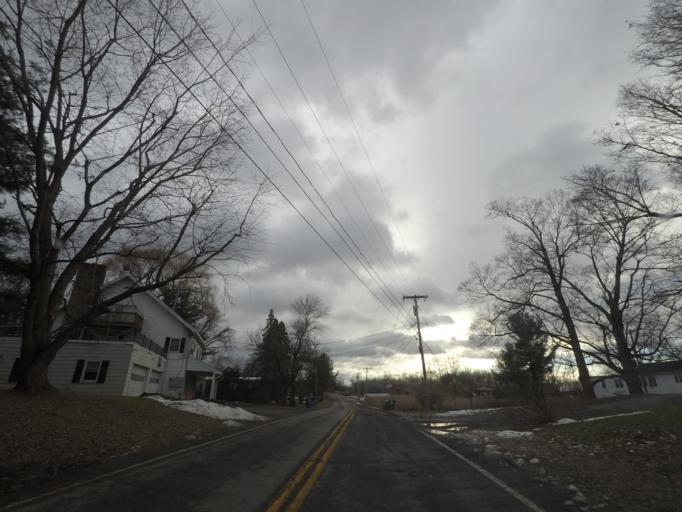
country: US
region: New York
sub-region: Rensselaer County
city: East Greenbush
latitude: 42.5961
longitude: -73.7197
